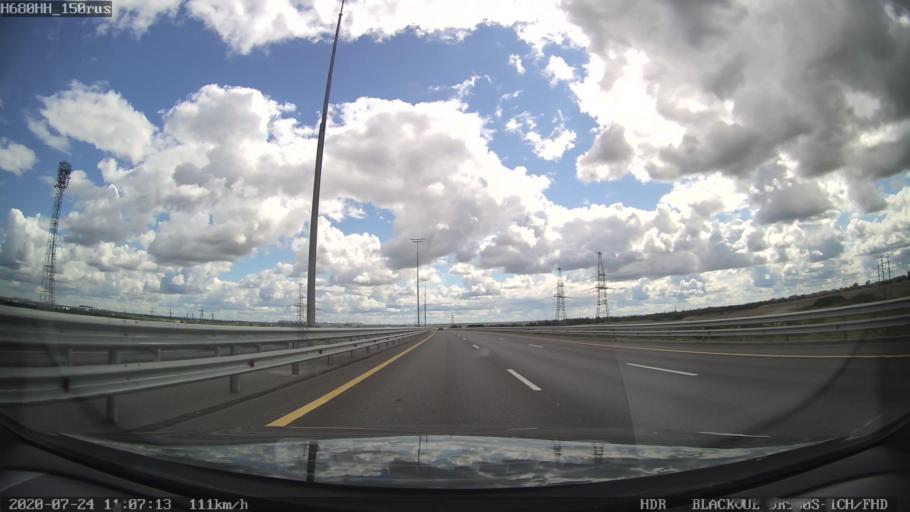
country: RU
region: St.-Petersburg
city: Pushkin
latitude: 59.7569
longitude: 30.3973
